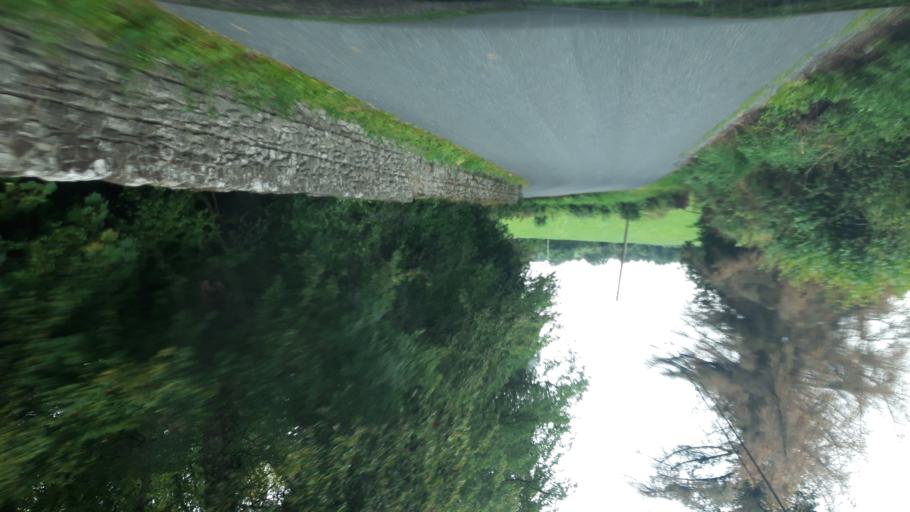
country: IE
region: Leinster
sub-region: Kilkenny
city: Ballyragget
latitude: 52.7251
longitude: -7.3995
